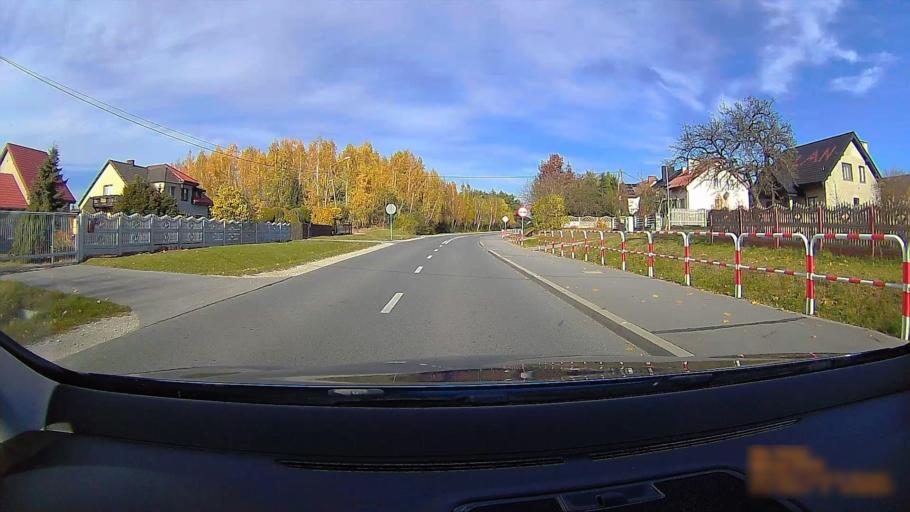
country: PL
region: Greater Poland Voivodeship
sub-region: Powiat kepinski
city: Kepno
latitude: 51.3223
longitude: 18.0135
